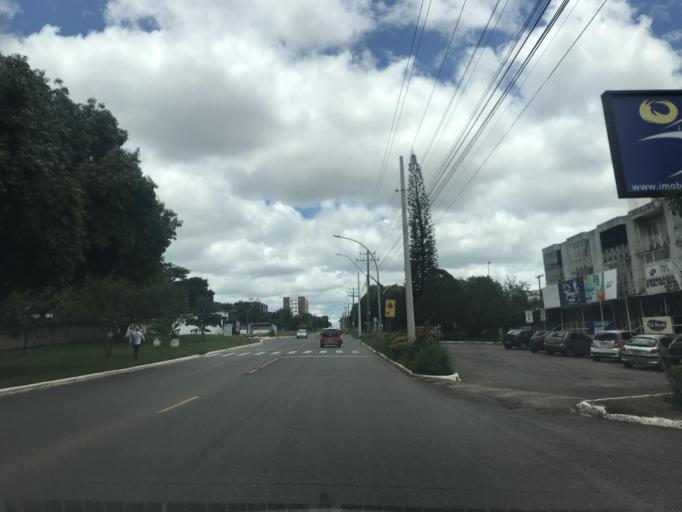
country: BR
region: Federal District
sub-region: Brasilia
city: Brasilia
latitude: -15.6546
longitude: -47.7945
